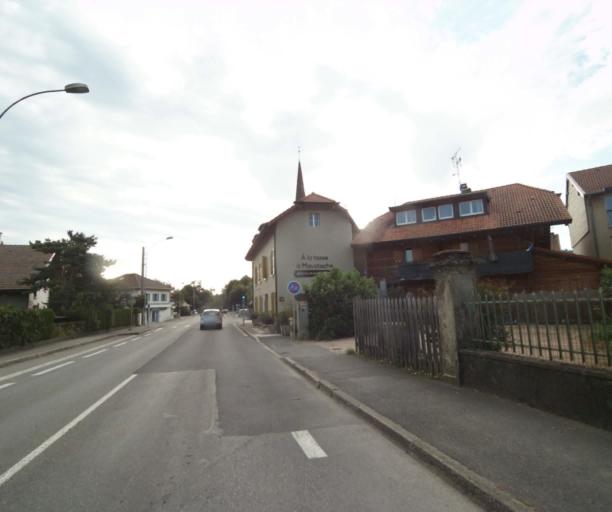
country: FR
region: Rhone-Alpes
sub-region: Departement de la Haute-Savoie
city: Thonon-les-Bains
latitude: 46.3826
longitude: 6.5038
